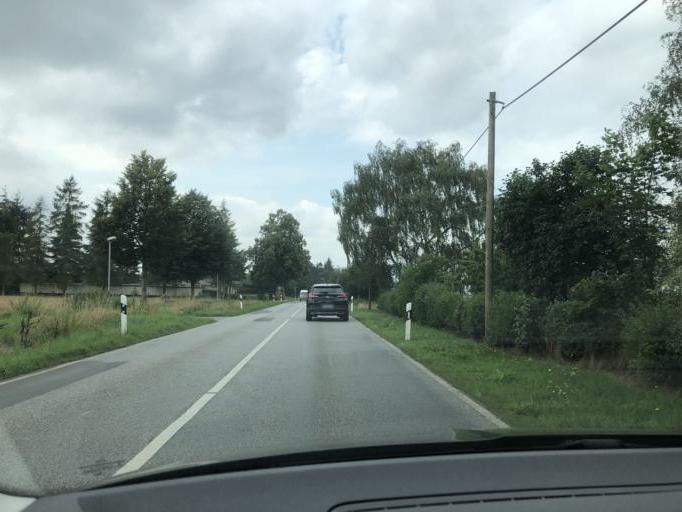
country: DE
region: Mecklenburg-Vorpommern
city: Klein Rogahn
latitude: 53.5707
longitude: 11.3412
